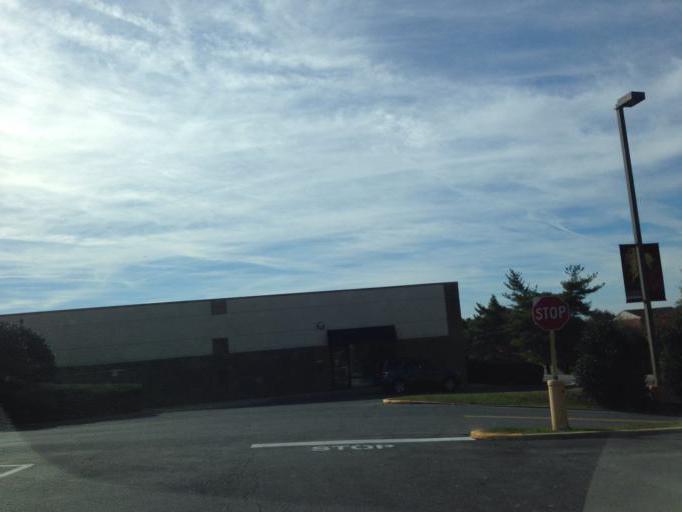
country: US
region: Maryland
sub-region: Howard County
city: Ellicott City
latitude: 39.2802
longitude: -76.8312
